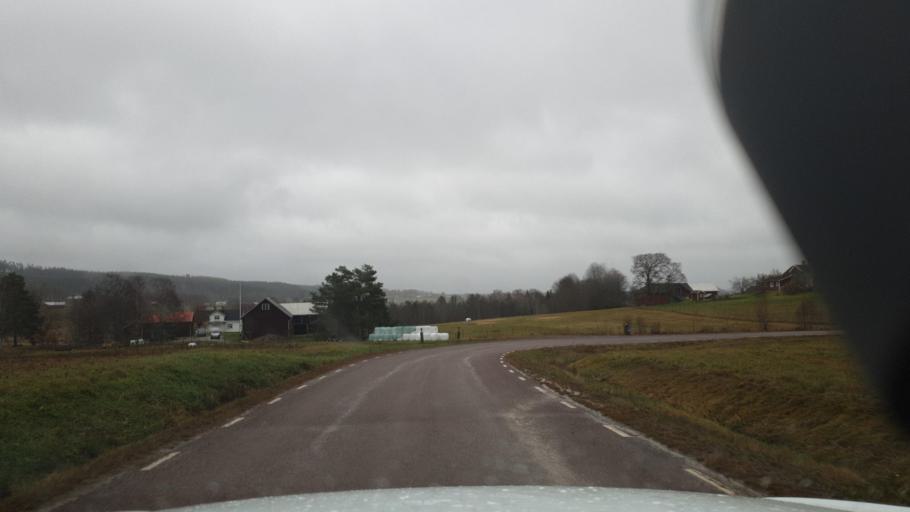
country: SE
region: Vaermland
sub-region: Sunne Kommun
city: Sunne
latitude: 59.7438
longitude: 13.0585
